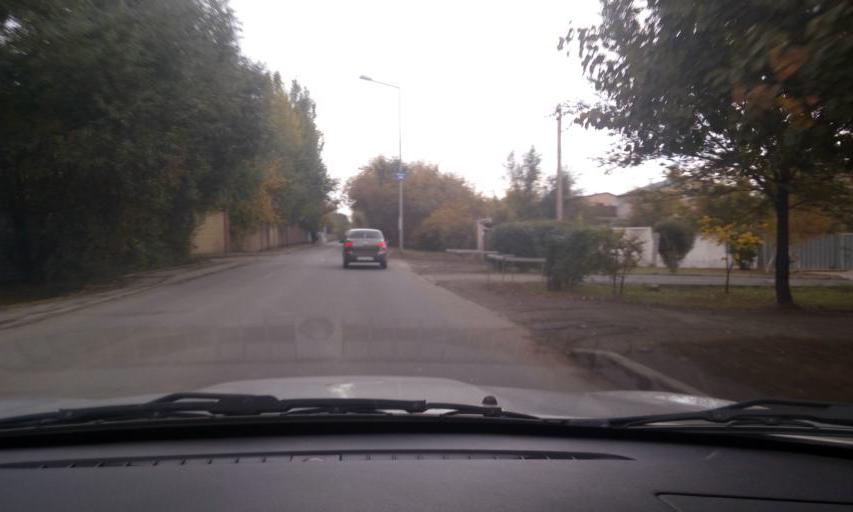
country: KZ
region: Astana Qalasy
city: Astana
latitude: 51.1409
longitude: 71.4325
